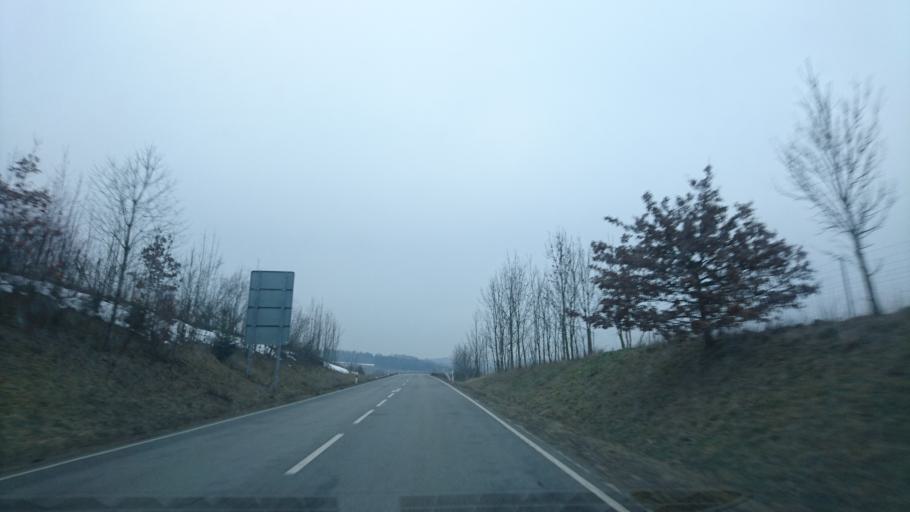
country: DE
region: Bavaria
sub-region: Lower Bavaria
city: Bad Griesbach
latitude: 48.4505
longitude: 13.1765
